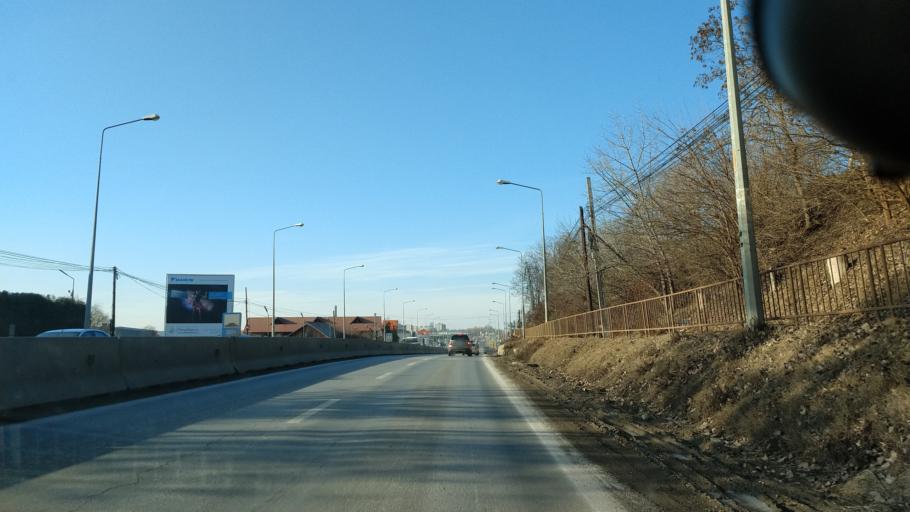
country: RO
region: Iasi
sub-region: Comuna Valea Lupului
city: Valea Lupului
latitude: 47.1737
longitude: 27.5082
